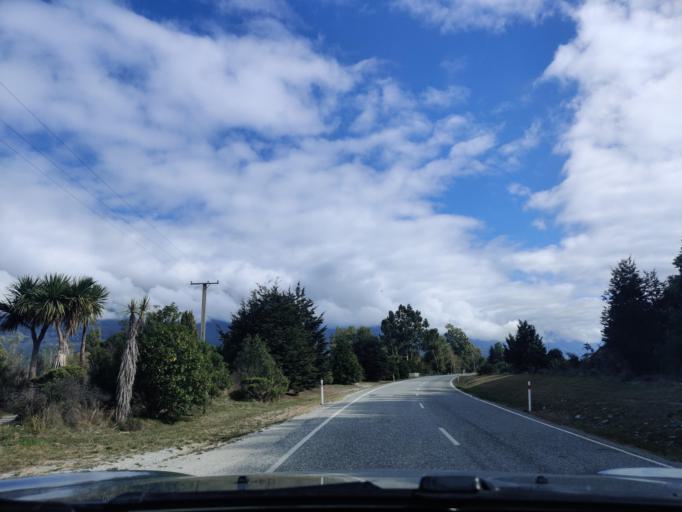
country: NZ
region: Otago
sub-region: Queenstown-Lakes District
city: Queenstown
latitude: -44.8577
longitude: 168.3928
